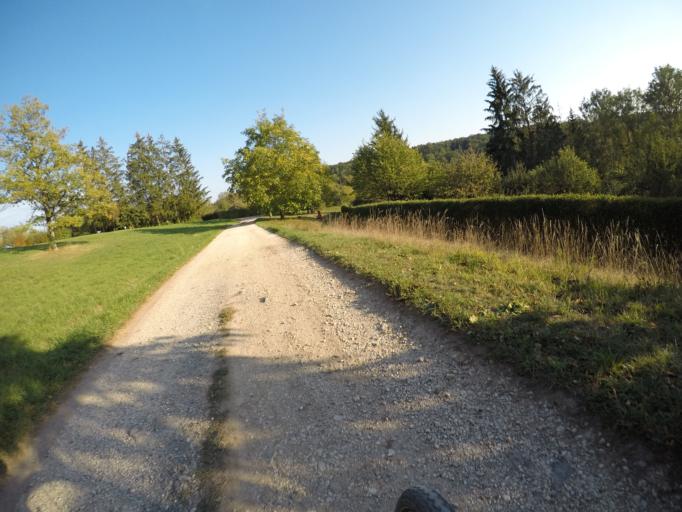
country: DE
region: Baden-Wuerttemberg
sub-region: Regierungsbezirk Stuttgart
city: Ostfildern
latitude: 48.7129
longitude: 9.2289
